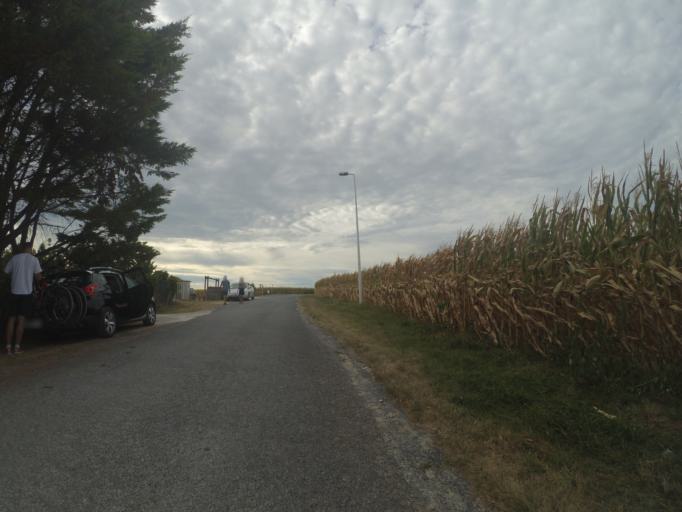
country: FR
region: Poitou-Charentes
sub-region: Departement de la Charente-Maritime
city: Meschers-sur-Gironde
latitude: 45.5521
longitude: -0.9198
